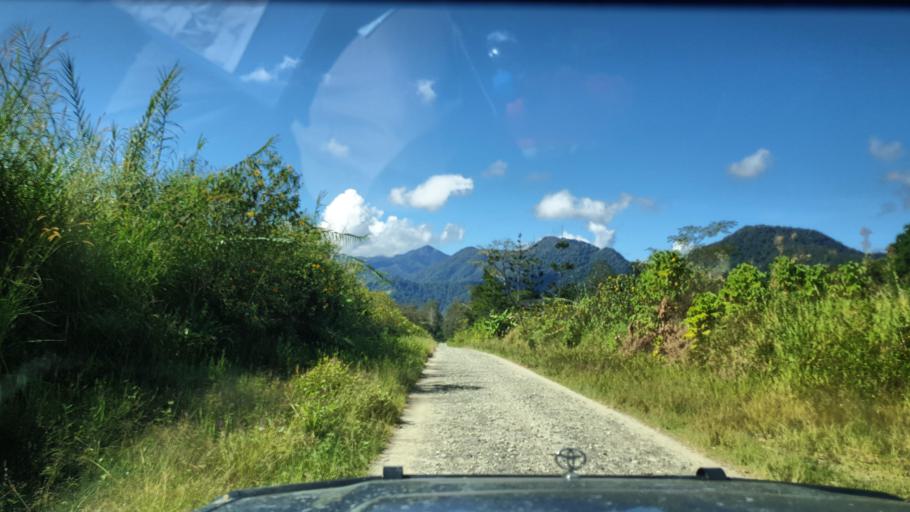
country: PG
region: Western Highlands
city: Rauna
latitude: -5.8111
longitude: 144.3777
